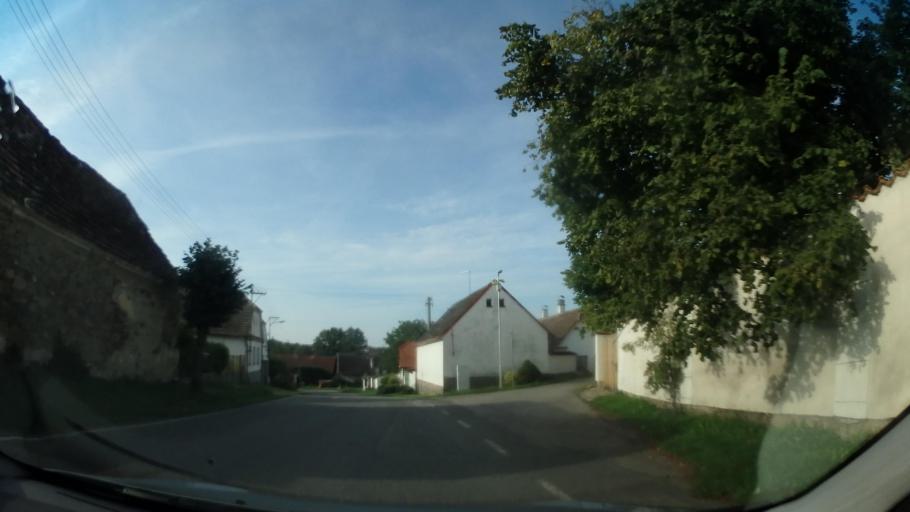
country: CZ
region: Jihocesky
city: Cimelice
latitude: 49.4760
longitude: 14.1518
